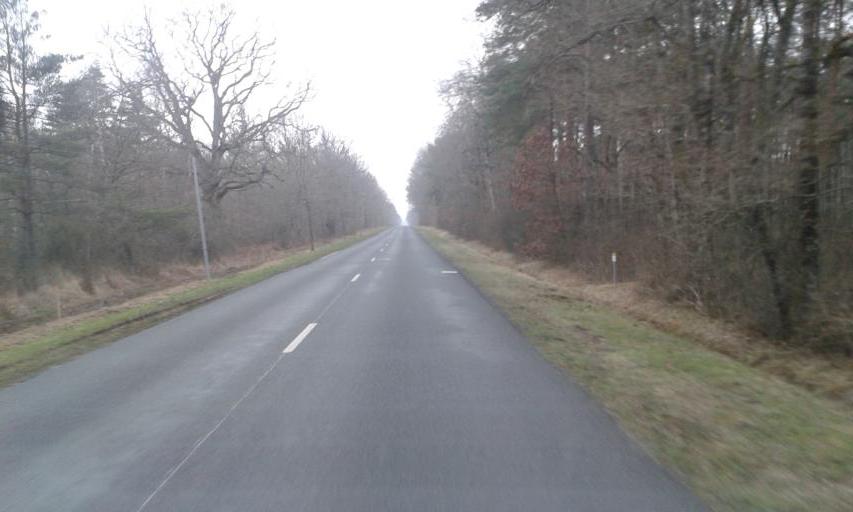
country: FR
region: Centre
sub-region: Departement du Loir-et-Cher
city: Saint-Laurent-Nouan
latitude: 47.6743
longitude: 1.6685
